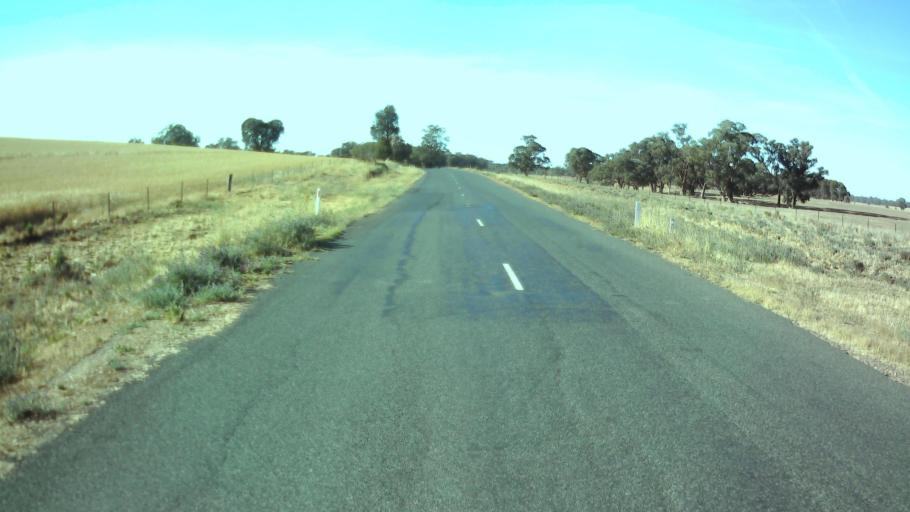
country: AU
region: New South Wales
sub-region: Weddin
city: Grenfell
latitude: -33.9704
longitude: 148.1407
